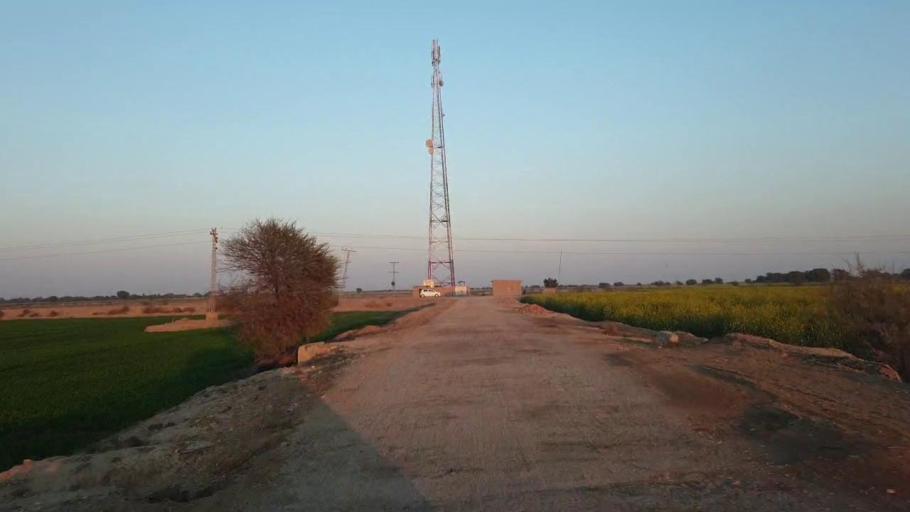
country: PK
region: Sindh
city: Shahpur Chakar
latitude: 26.1687
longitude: 68.5568
